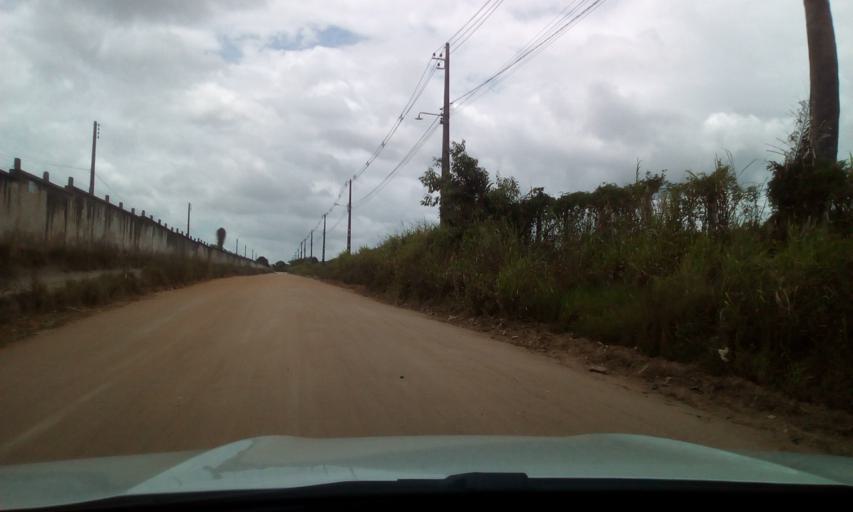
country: BR
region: Paraiba
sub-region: Bayeux
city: Bayeux
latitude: -7.1371
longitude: -34.9515
